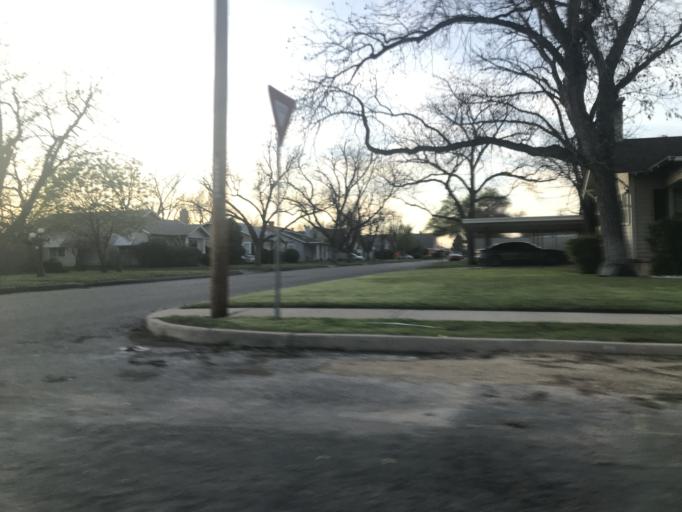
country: US
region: Texas
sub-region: Tom Green County
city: San Angelo
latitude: 31.4519
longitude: -100.4564
